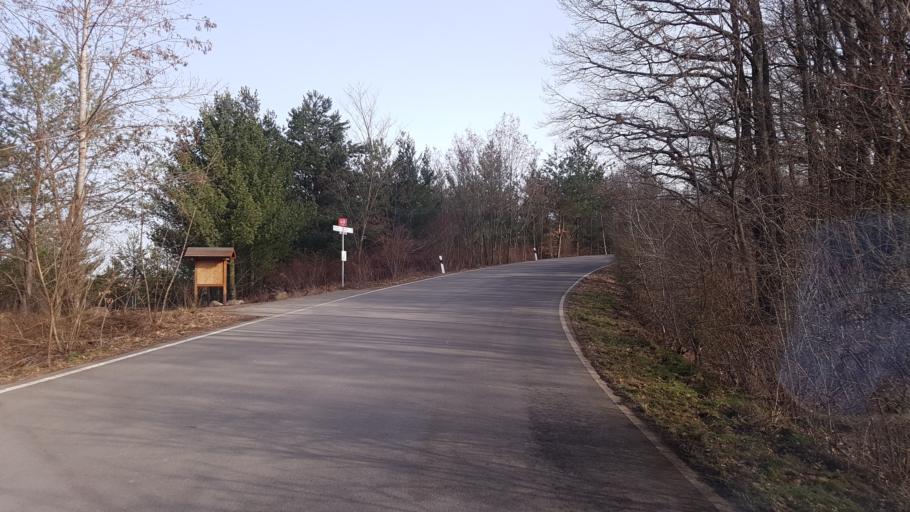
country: DE
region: Brandenburg
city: Schipkau
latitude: 51.5300
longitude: 13.8266
